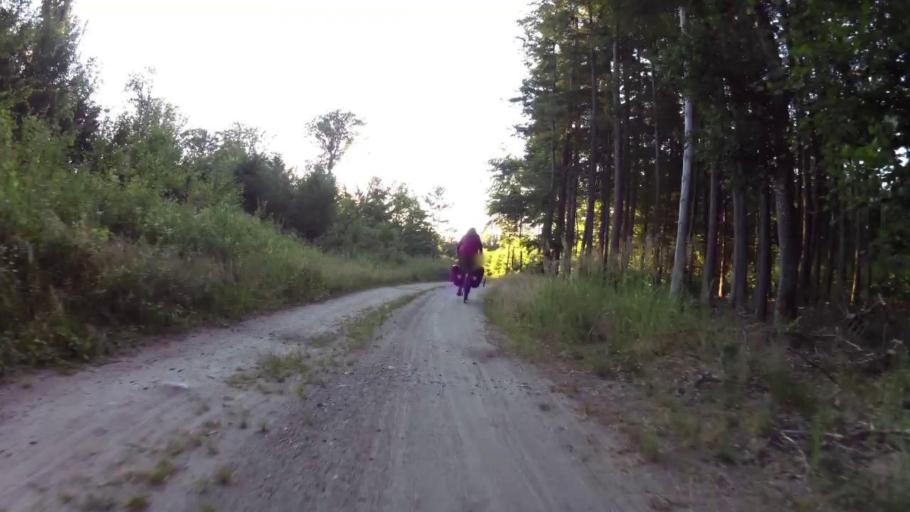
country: PL
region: West Pomeranian Voivodeship
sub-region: Powiat lobeski
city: Lobez
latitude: 53.7497
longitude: 15.6381
